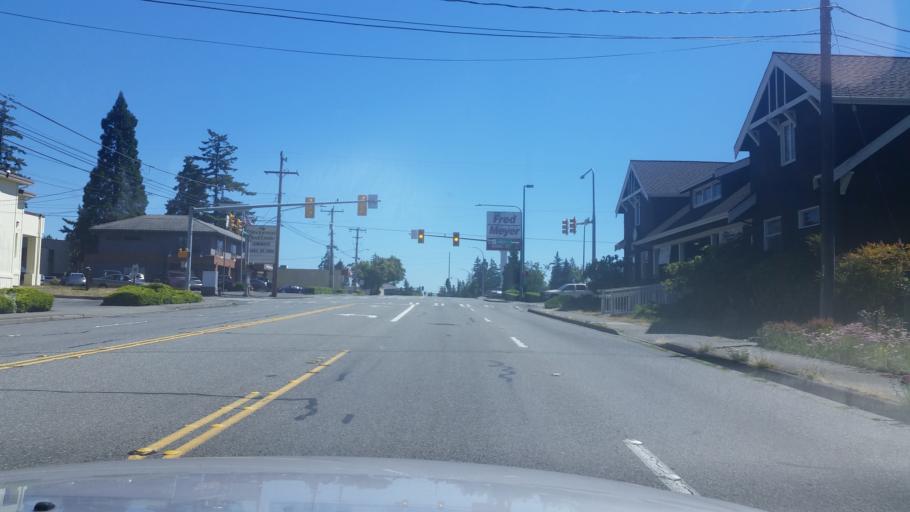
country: US
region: Washington
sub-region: King County
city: Shoreline
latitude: 47.7632
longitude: -122.3496
